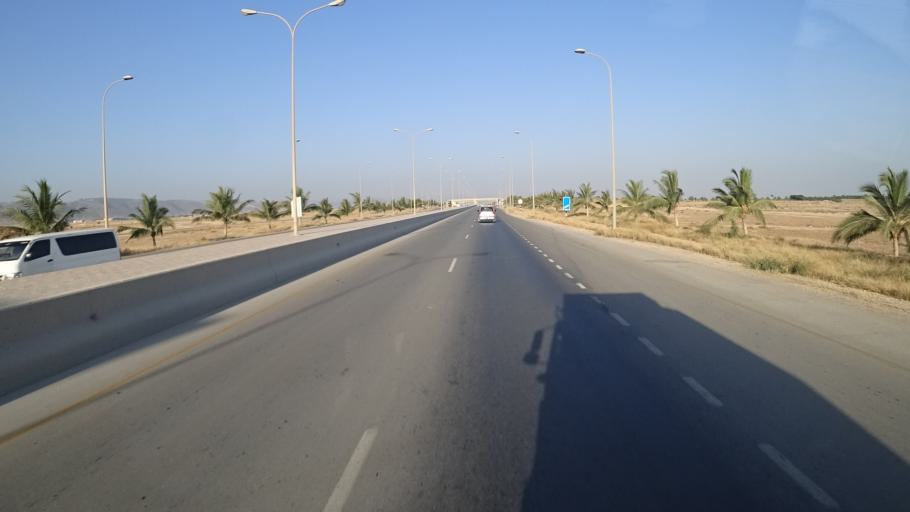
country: OM
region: Zufar
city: Salalah
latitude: 17.0549
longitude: 54.0750
